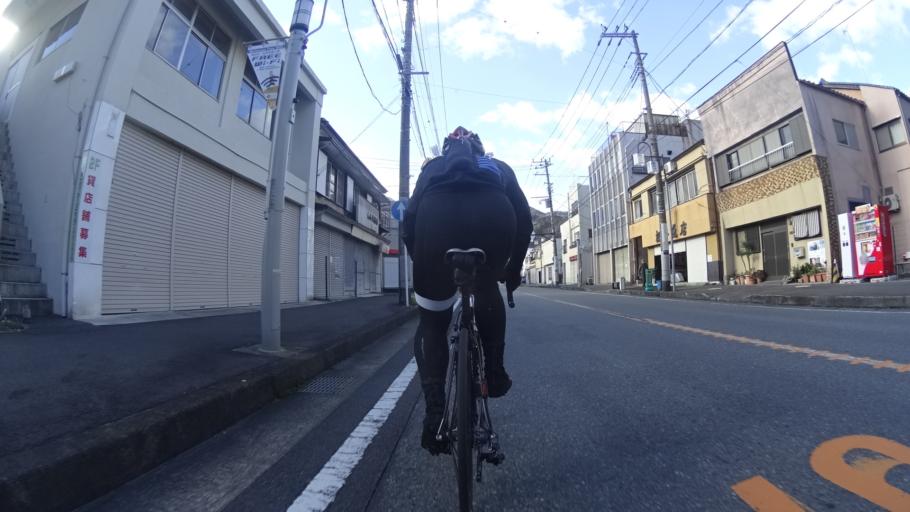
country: JP
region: Kanagawa
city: Yugawara
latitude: 35.1441
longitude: 139.1002
